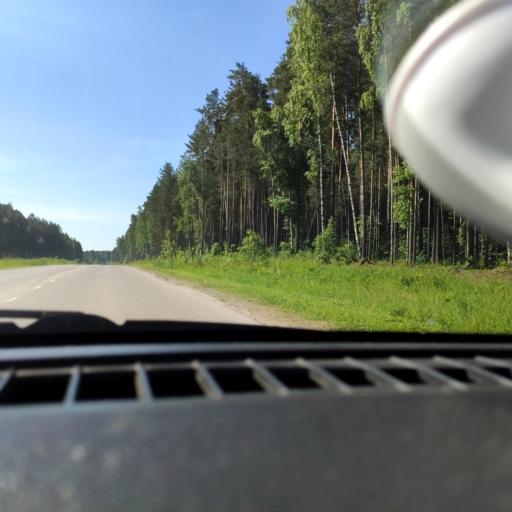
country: RU
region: Perm
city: Overyata
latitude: 58.0040
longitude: 55.8776
